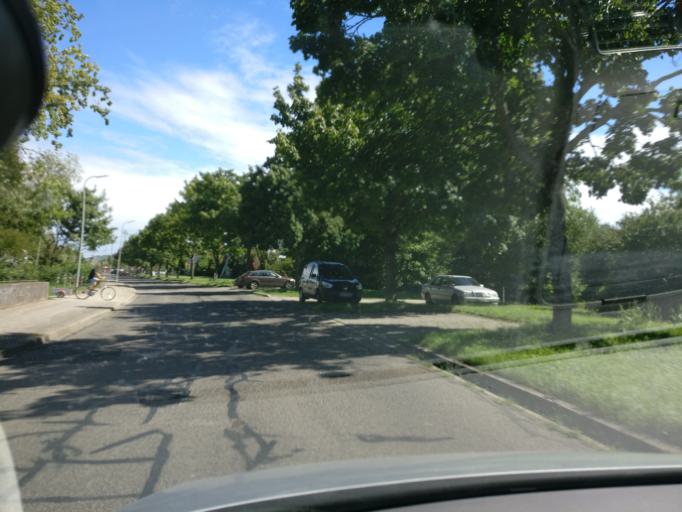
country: DE
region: Baden-Wuerttemberg
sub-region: Karlsruhe Region
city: Karlsruhe
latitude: 49.0219
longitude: 8.4540
